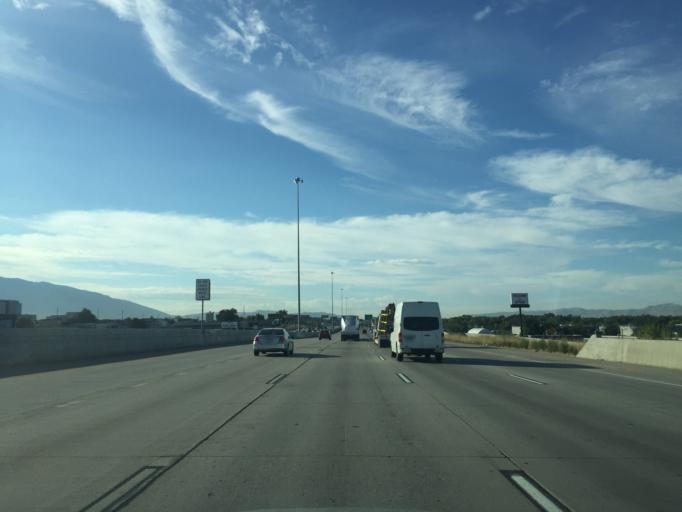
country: US
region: Utah
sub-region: Salt Lake County
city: Murray
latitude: 40.6739
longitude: -111.9016
